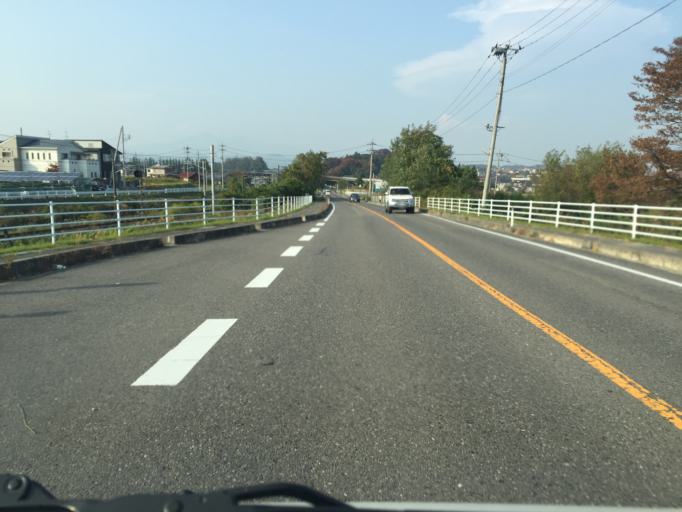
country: JP
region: Fukushima
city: Koriyama
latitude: 37.4391
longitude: 140.3915
